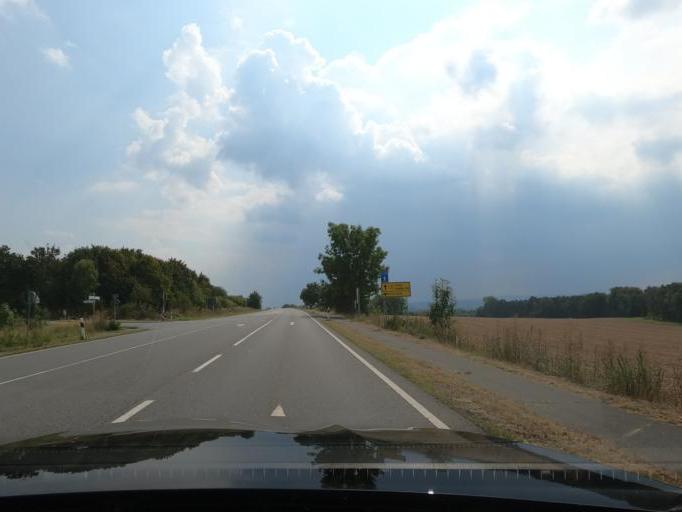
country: DE
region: Lower Saxony
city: Heere
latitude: 52.0762
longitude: 10.2559
